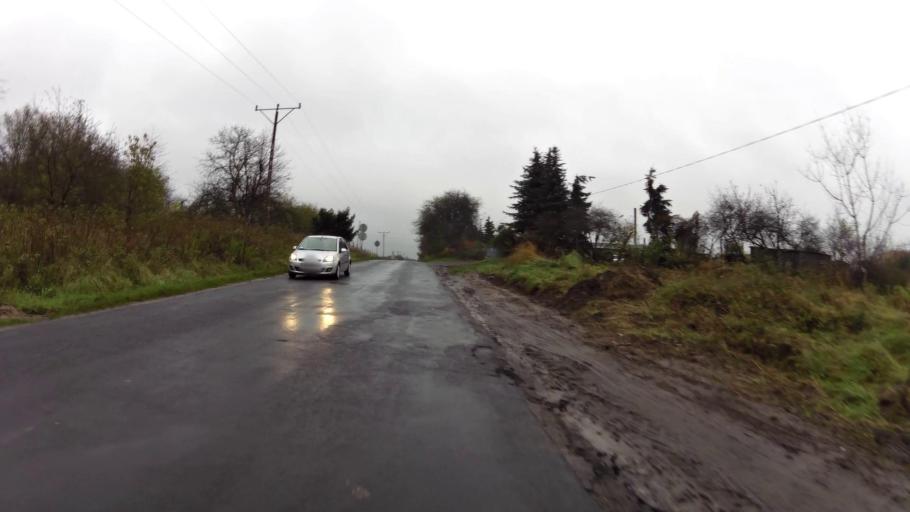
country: PL
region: West Pomeranian Voivodeship
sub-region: Powiat gryfinski
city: Gryfino
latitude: 53.2410
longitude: 14.5076
